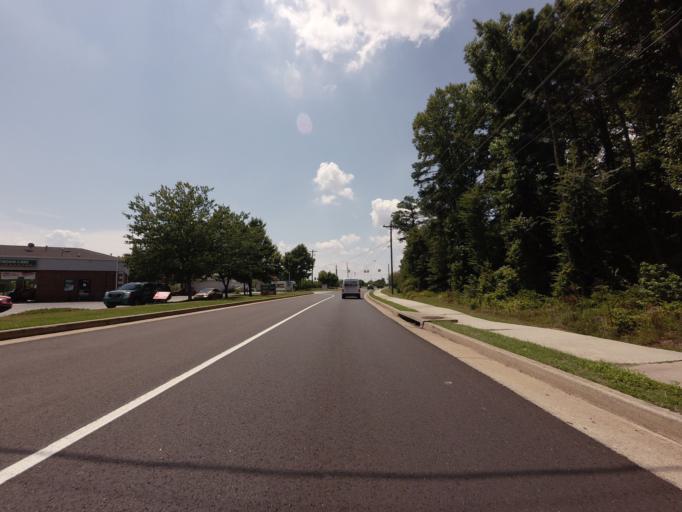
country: US
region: Georgia
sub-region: Fulton County
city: Johns Creek
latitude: 34.0581
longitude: -84.2312
